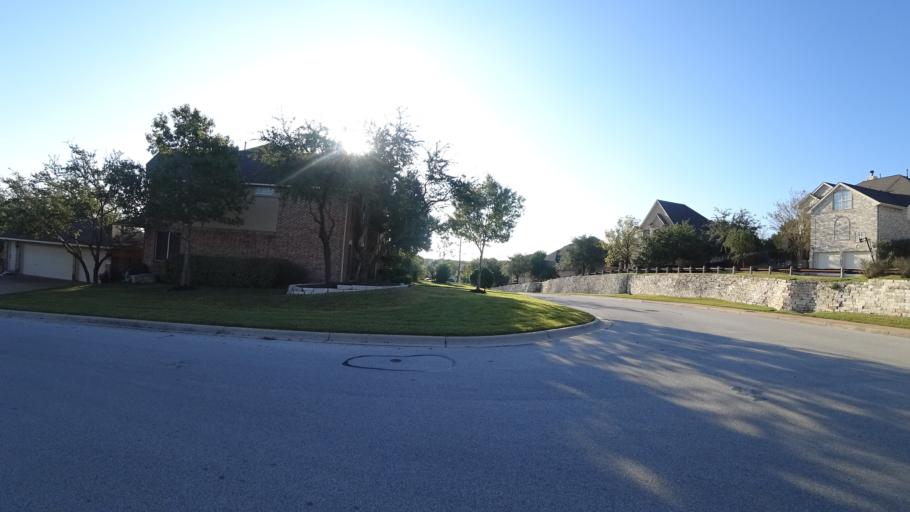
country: US
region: Texas
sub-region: Travis County
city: Hudson Bend
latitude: 30.3735
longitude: -97.8841
